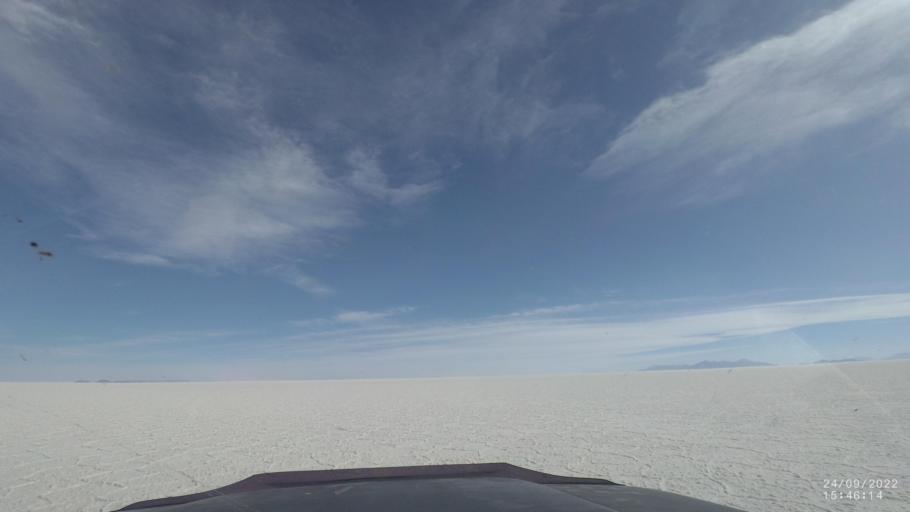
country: BO
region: Potosi
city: Colchani
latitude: -20.2651
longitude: -67.2222
